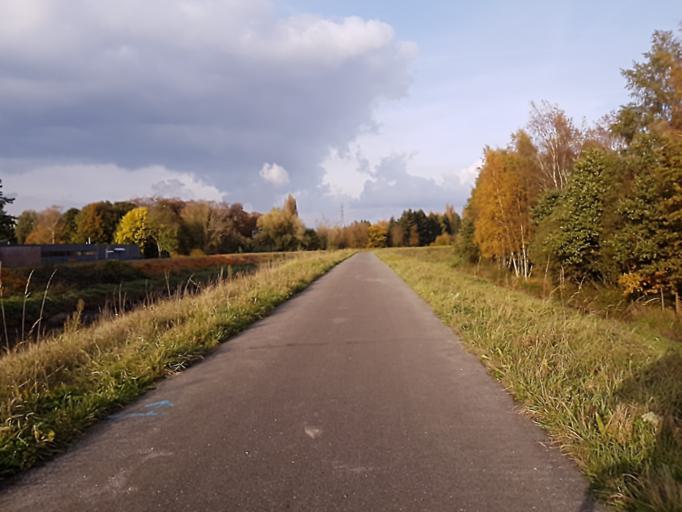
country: BE
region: Flanders
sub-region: Provincie Antwerpen
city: Lier
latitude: 51.1471
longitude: 4.5789
